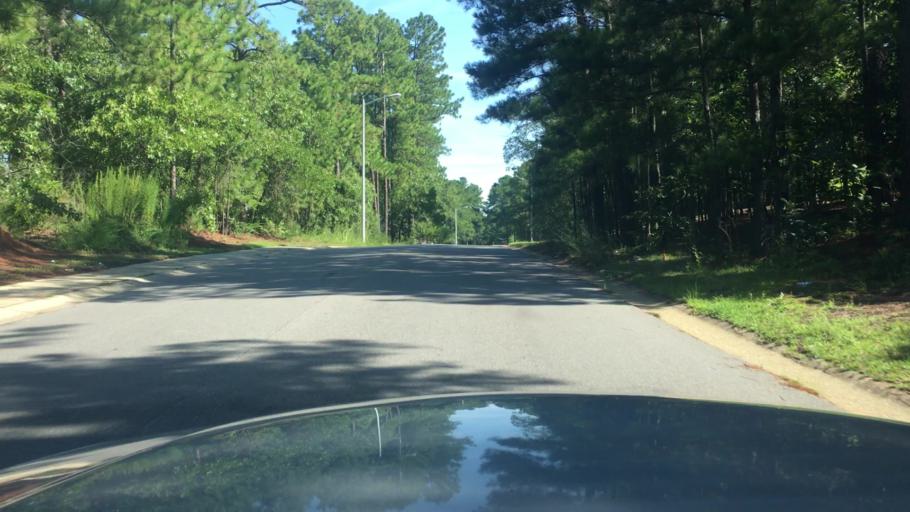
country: US
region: North Carolina
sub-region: Cumberland County
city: Fayetteville
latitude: 35.1101
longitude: -78.9106
